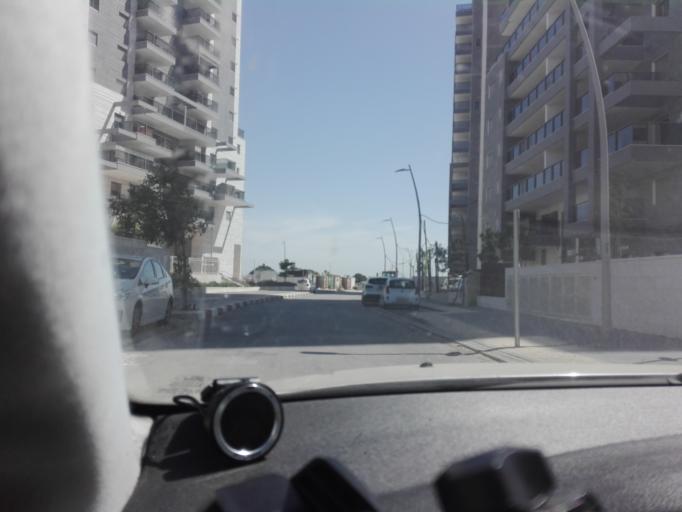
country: IL
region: Central District
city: Bene 'Ayish
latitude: 31.7255
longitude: 34.7380
